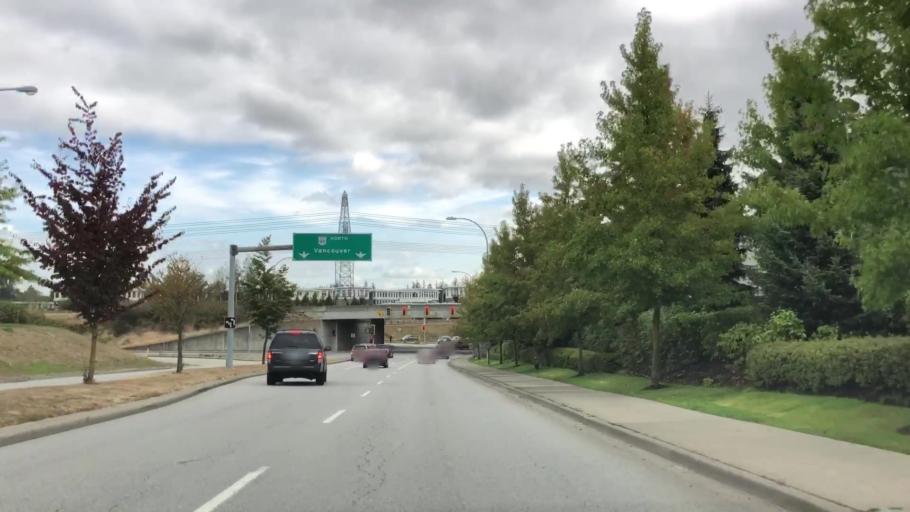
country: CA
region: British Columbia
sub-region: Greater Vancouver Regional District
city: White Rock
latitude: 49.0605
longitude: -122.8067
